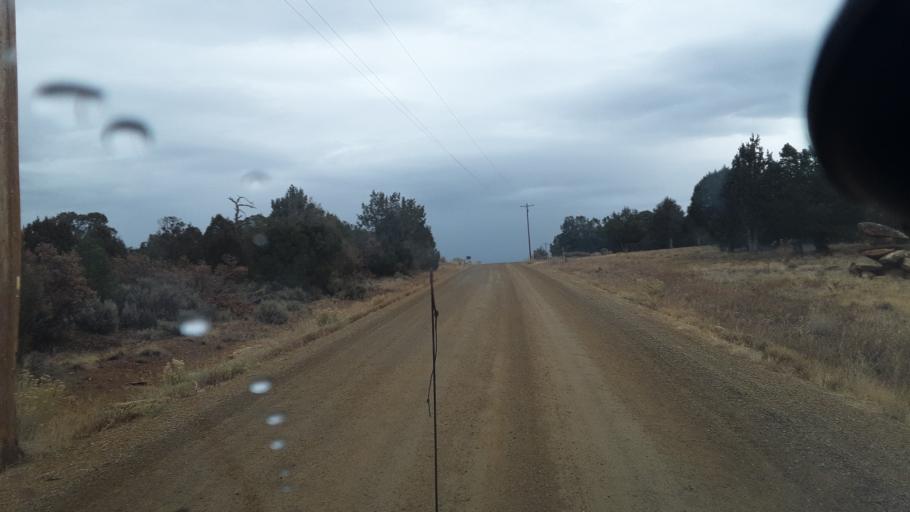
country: US
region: Colorado
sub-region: Montezuma County
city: Mancos
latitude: 37.1984
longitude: -108.1343
